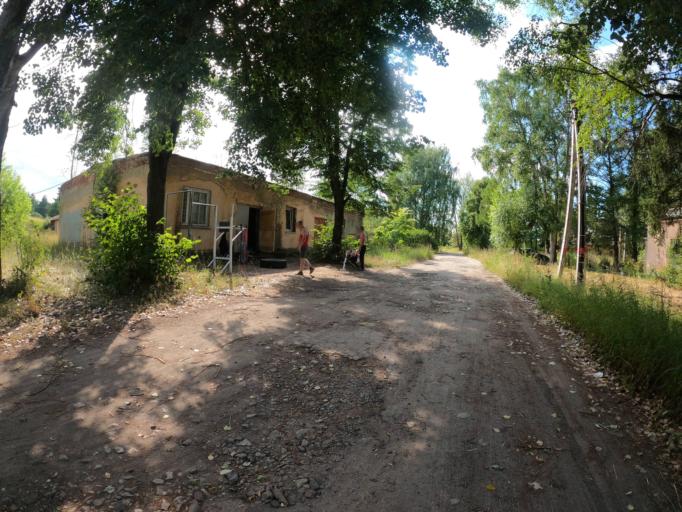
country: RU
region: Moskovskaya
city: Konobeyevo
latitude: 55.3914
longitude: 38.7087
